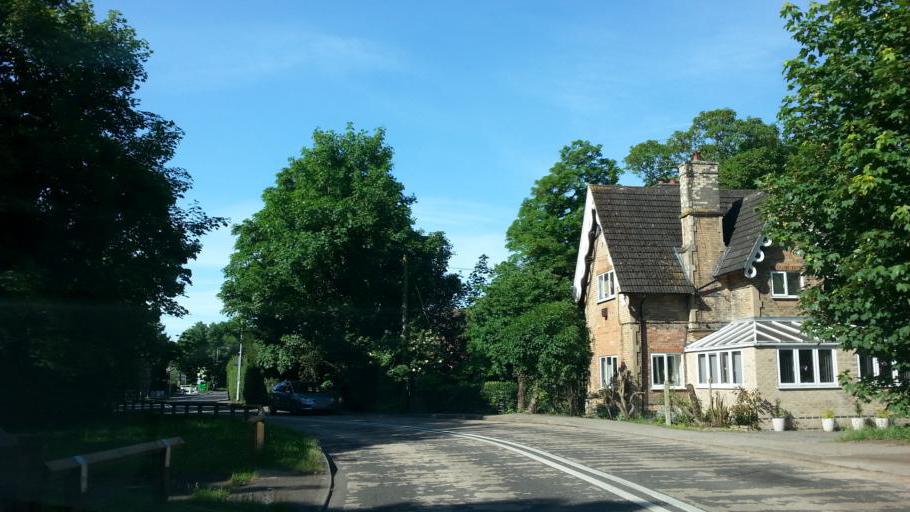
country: GB
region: England
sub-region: Nottinghamshire
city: Southwell
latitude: 53.0793
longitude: -0.9407
